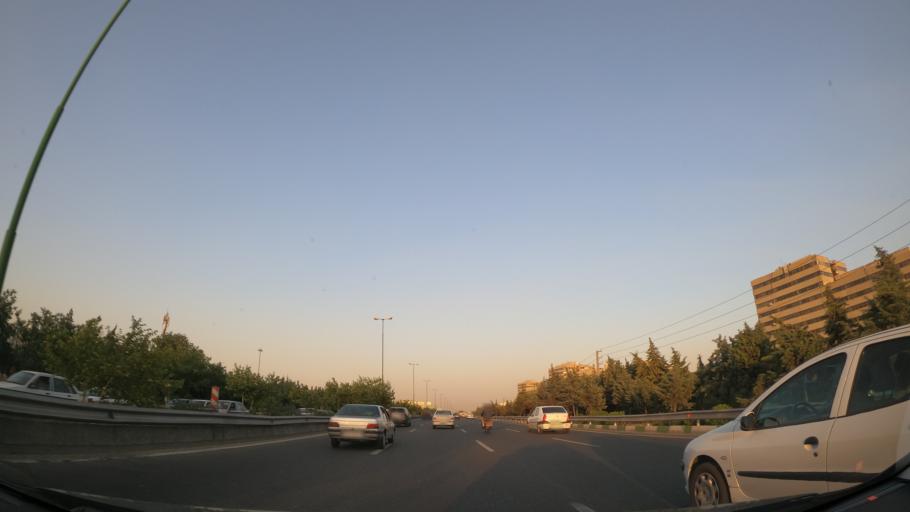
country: IR
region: Tehran
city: Tehran
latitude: 35.7165
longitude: 51.3149
